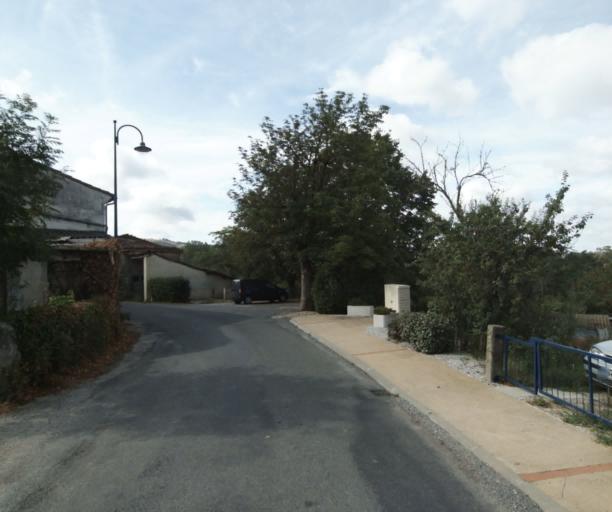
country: FR
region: Midi-Pyrenees
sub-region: Departement du Tarn
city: Soreze
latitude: 43.4707
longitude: 2.0777
